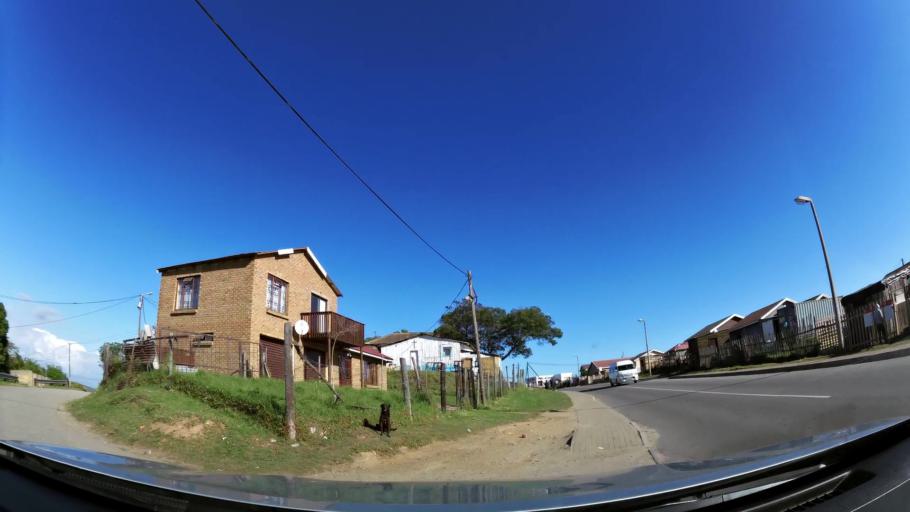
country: ZA
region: Western Cape
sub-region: Eden District Municipality
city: Knysna
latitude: -34.0279
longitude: 23.0675
